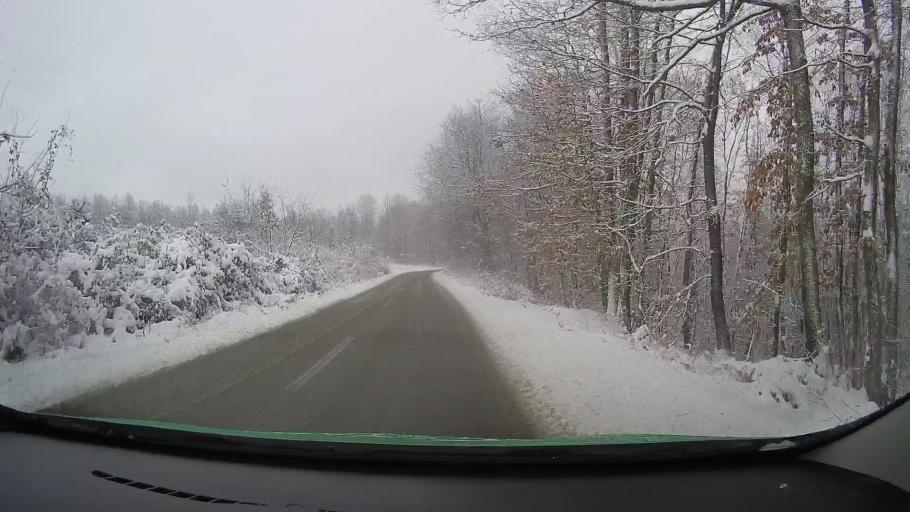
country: RO
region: Hunedoara
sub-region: Comuna Teliucu Inferior
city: Teliucu Inferior
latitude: 45.6813
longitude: 22.9118
